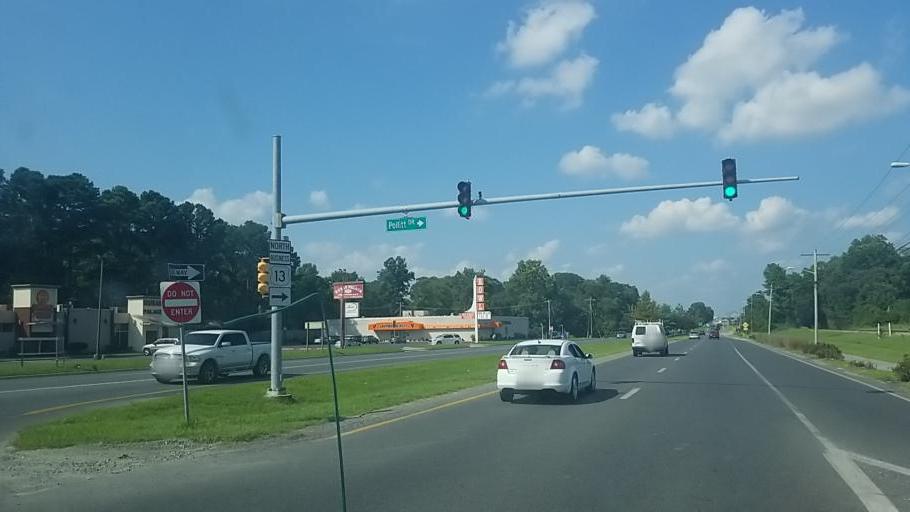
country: US
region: Maryland
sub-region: Wicomico County
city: Fruitland
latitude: 38.3311
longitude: -75.6123
